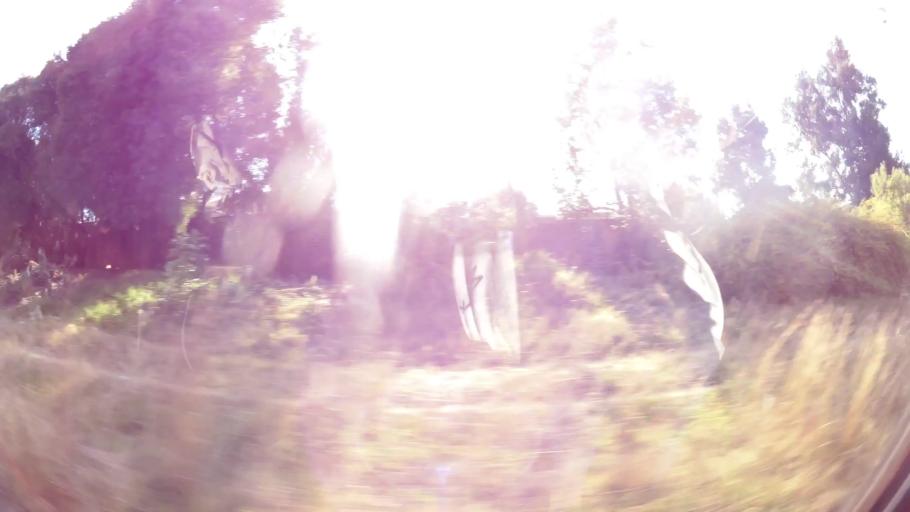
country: ZA
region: Gauteng
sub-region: City of Johannesburg Metropolitan Municipality
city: Roodepoort
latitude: -26.1020
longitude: 27.9497
